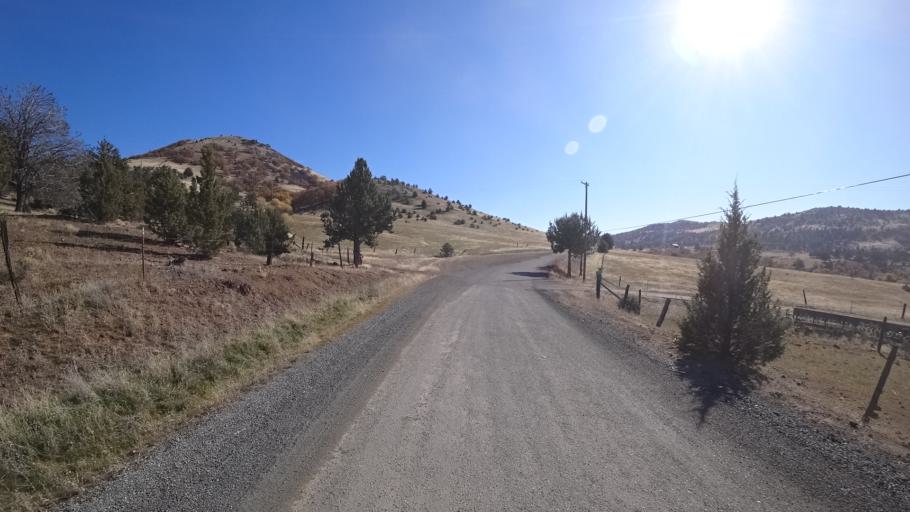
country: US
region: California
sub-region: Siskiyou County
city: Montague
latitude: 41.8012
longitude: -122.3688
